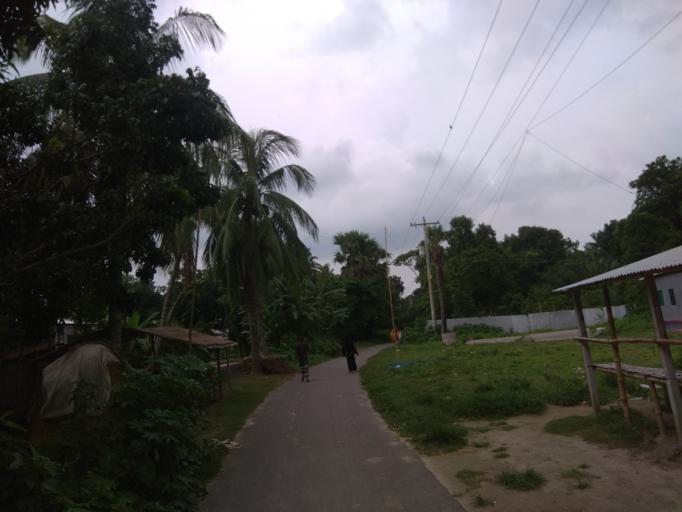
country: BD
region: Dhaka
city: Dohar
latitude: 23.4886
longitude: 89.9898
